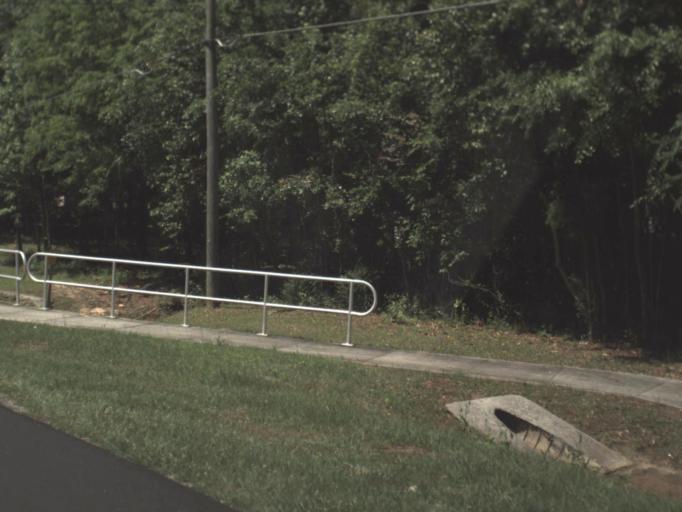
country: US
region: Florida
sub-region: Jackson County
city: Marianna
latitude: 30.7863
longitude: -85.2259
